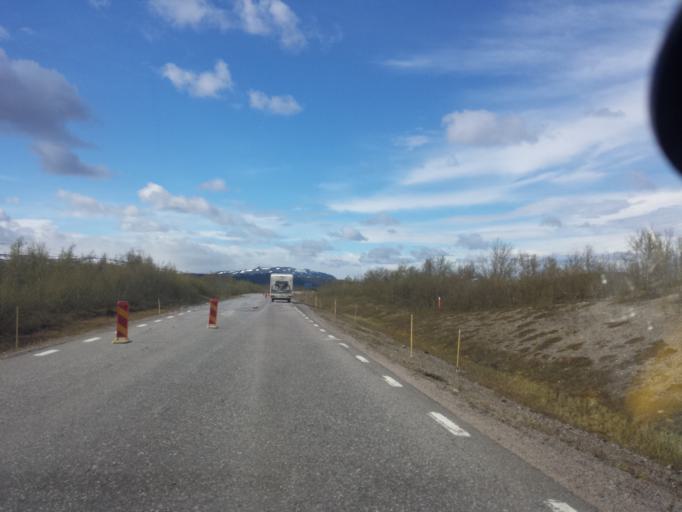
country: SE
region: Norrbotten
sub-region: Kiruna Kommun
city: Kiruna
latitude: 68.0057
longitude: 19.8509
